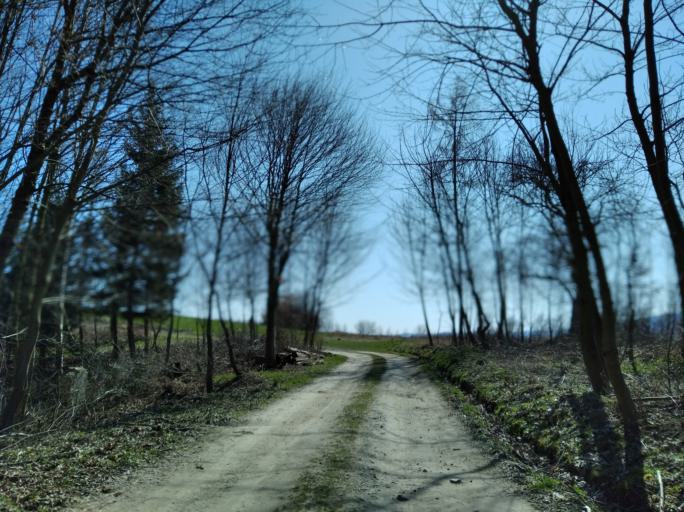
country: PL
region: Subcarpathian Voivodeship
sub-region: Powiat strzyzowski
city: Strzyzow
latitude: 49.8552
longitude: 21.8099
